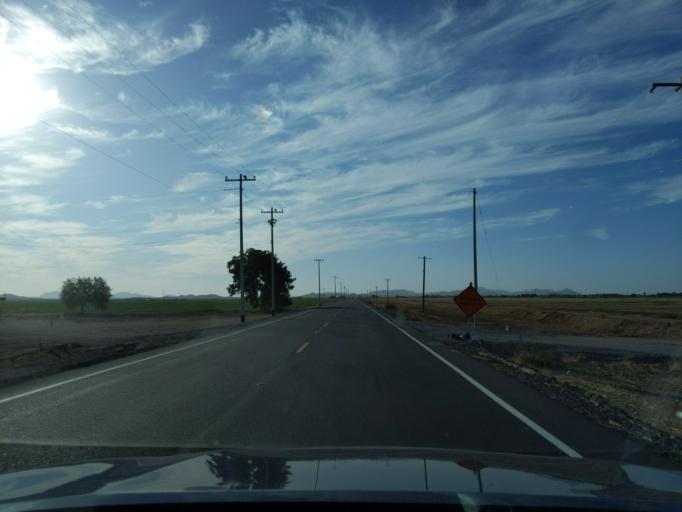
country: US
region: Arizona
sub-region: Pinal County
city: Florence
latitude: 33.1184
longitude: -111.4218
